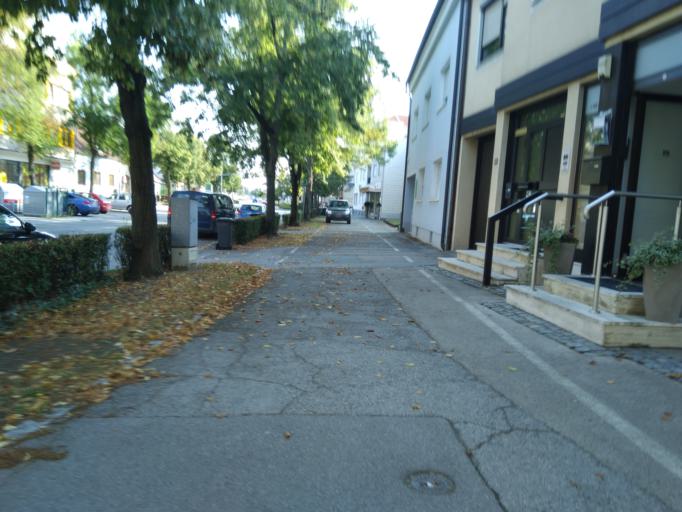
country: AT
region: Lower Austria
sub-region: Politischer Bezirk Ganserndorf
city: Ganserndorf
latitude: 48.3416
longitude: 16.7184
